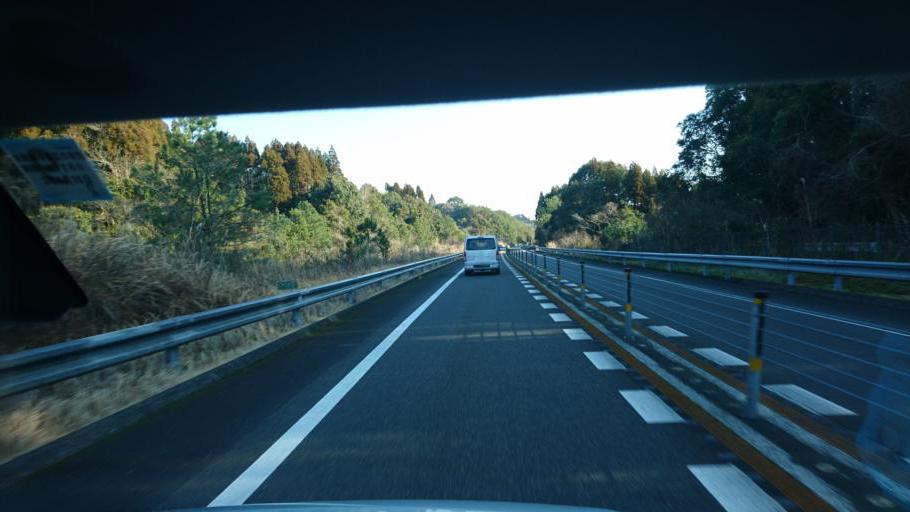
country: JP
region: Miyazaki
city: Tsuma
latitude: 32.0112
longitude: 131.3804
